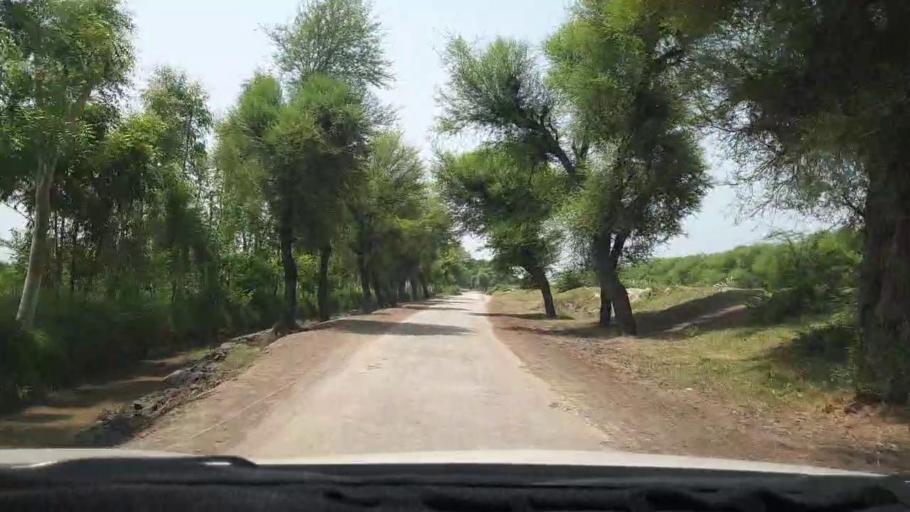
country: PK
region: Sindh
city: Dokri
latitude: 27.3200
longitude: 68.1069
